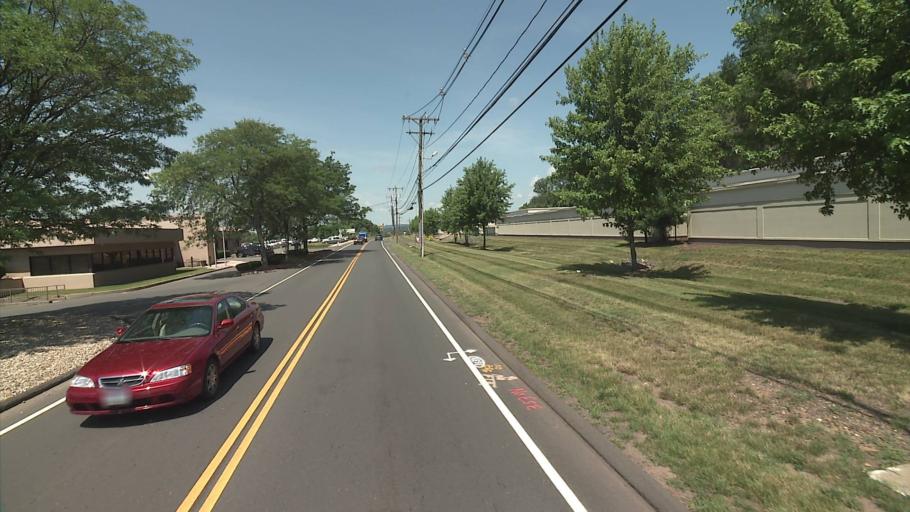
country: US
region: Connecticut
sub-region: Hartford County
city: Plainville
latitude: 41.6714
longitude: -72.8327
